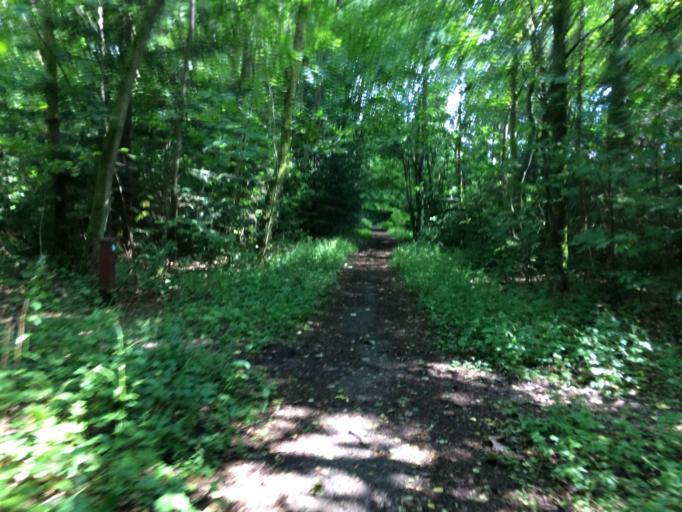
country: DK
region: Central Jutland
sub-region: Holstebro Kommune
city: Ulfborg
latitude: 56.2835
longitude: 8.1751
